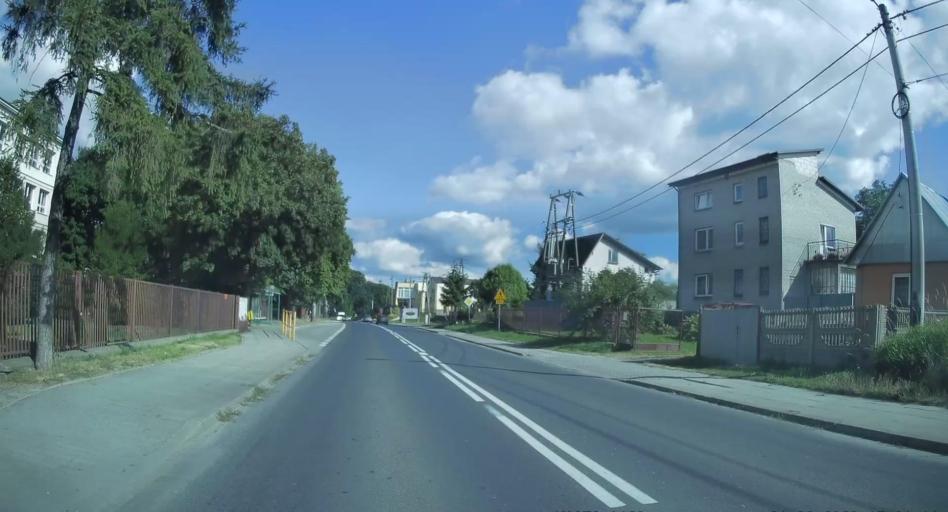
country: PL
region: Swietokrzyskie
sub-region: Powiat kielecki
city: Bodzentyn
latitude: 50.9423
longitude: 20.9462
